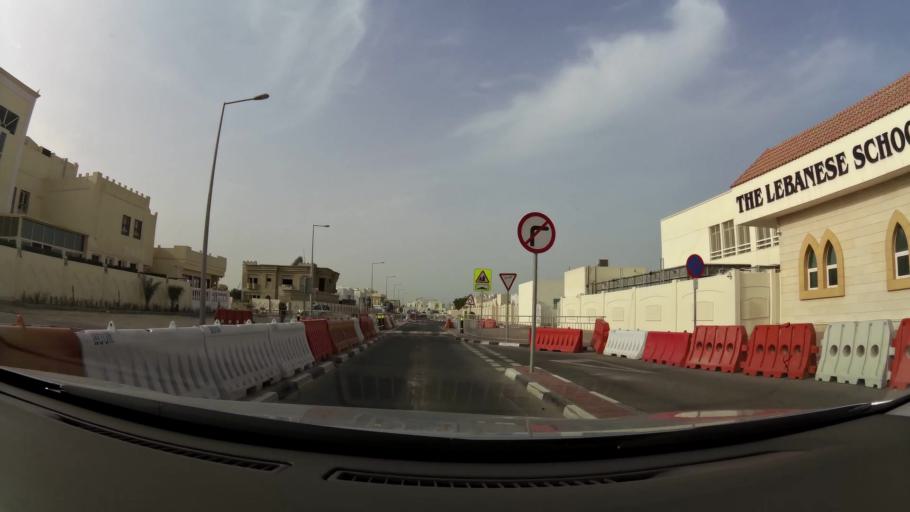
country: QA
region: Baladiyat ad Dawhah
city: Doha
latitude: 25.3278
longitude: 51.5204
